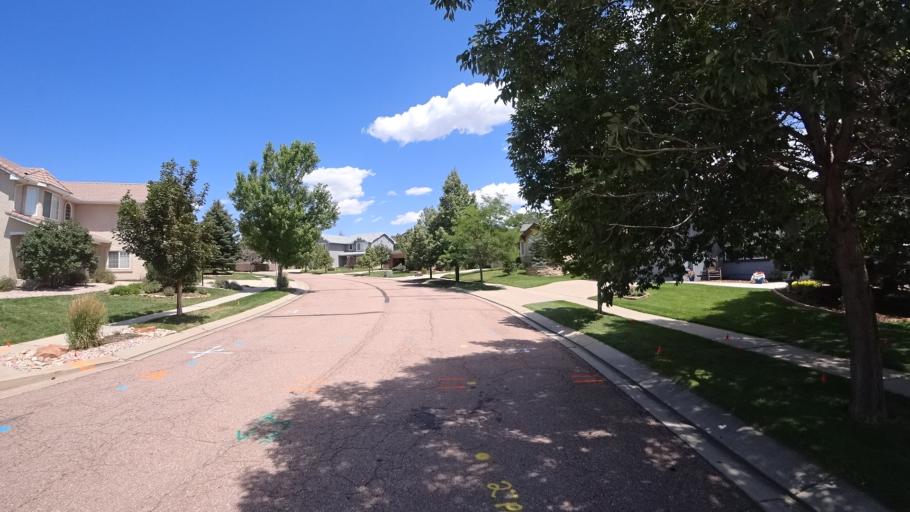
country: US
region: Colorado
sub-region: El Paso County
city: Black Forest
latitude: 38.9691
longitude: -104.7664
